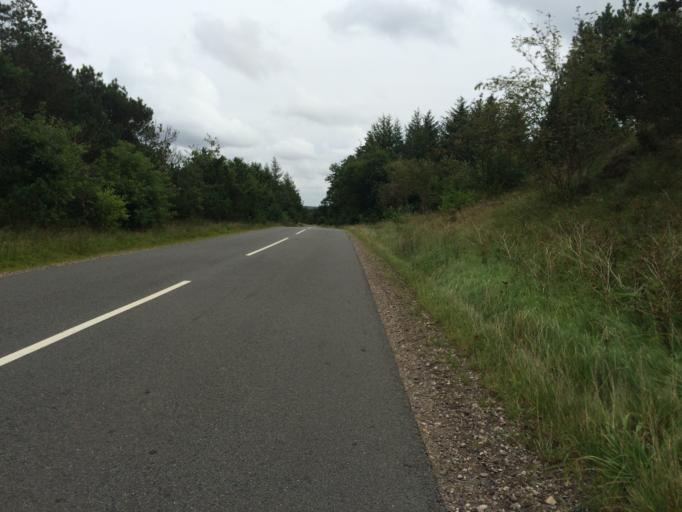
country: DK
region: Central Jutland
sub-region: Holstebro Kommune
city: Ulfborg
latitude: 56.2236
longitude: 8.3847
